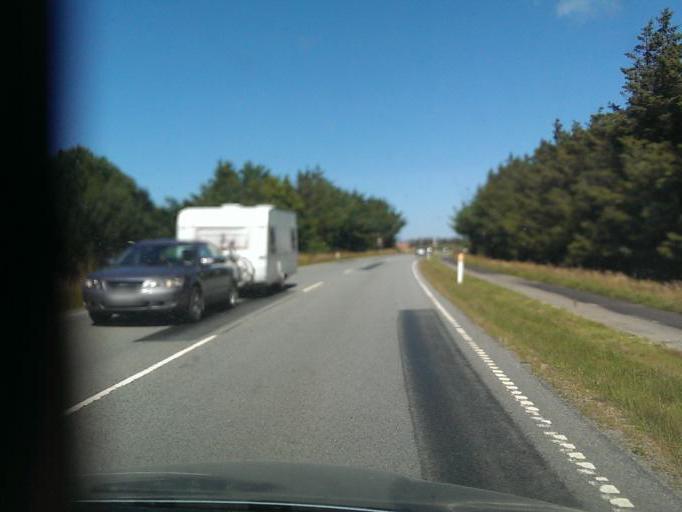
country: DK
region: North Denmark
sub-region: Jammerbugt Kommune
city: Pandrup
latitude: 57.3588
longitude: 9.7082
